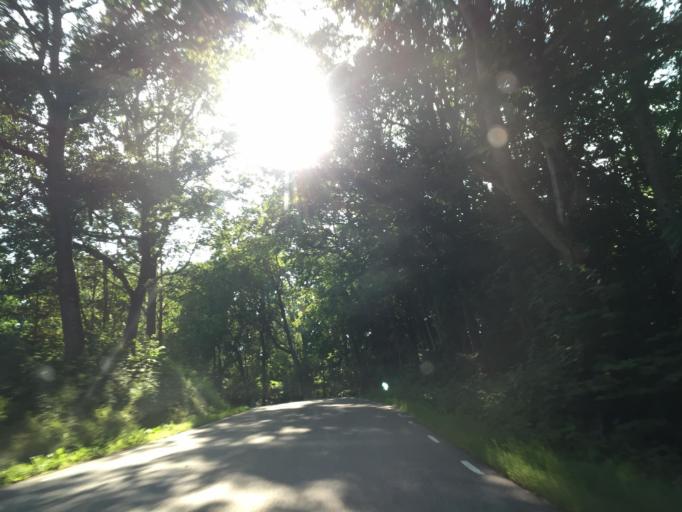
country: SE
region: Vaestra Goetaland
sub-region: Lilla Edets Kommun
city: Lilla Edet
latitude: 58.1824
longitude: 12.1103
